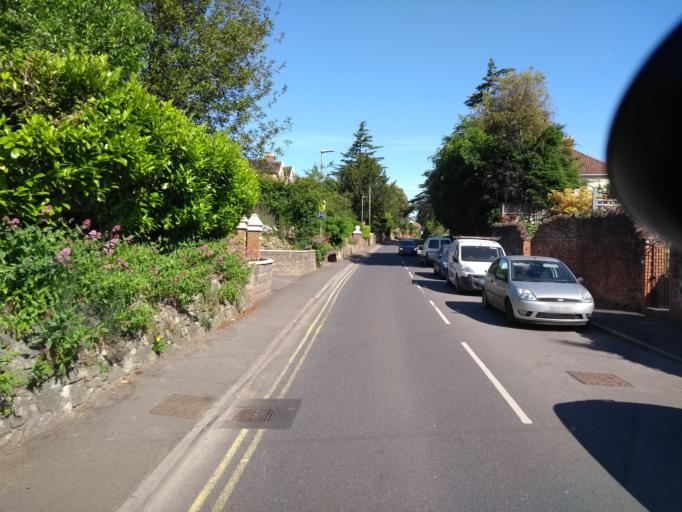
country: GB
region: England
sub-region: Somerset
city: Bridgwater
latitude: 51.1302
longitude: -3.0211
